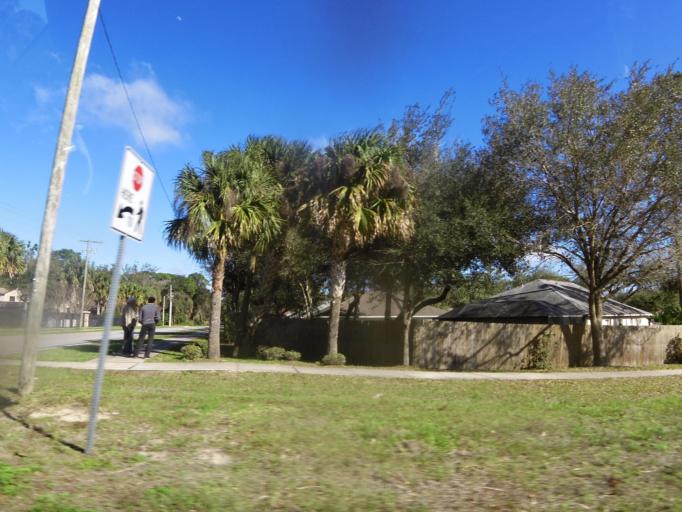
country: US
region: Florida
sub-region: Brevard County
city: Port Saint John
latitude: 28.5429
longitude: -80.8064
